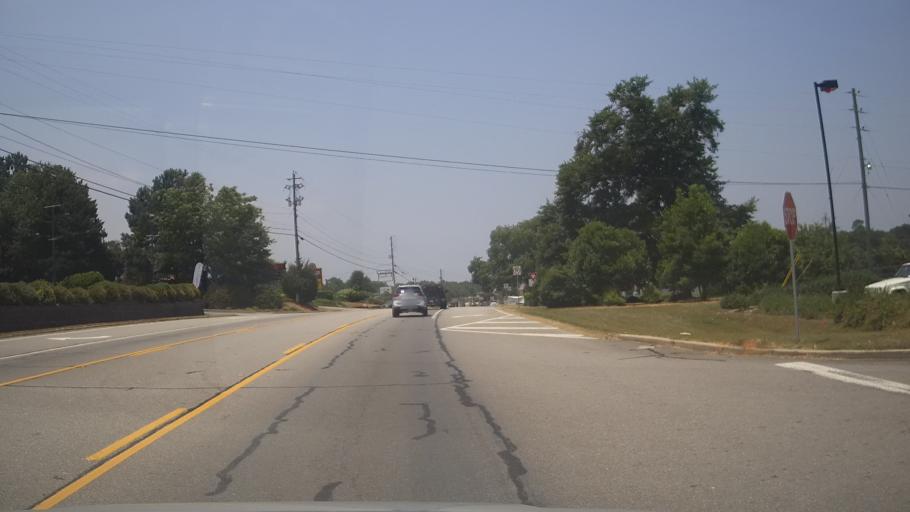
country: US
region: Georgia
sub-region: Hart County
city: Royston
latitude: 34.2845
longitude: -83.1240
